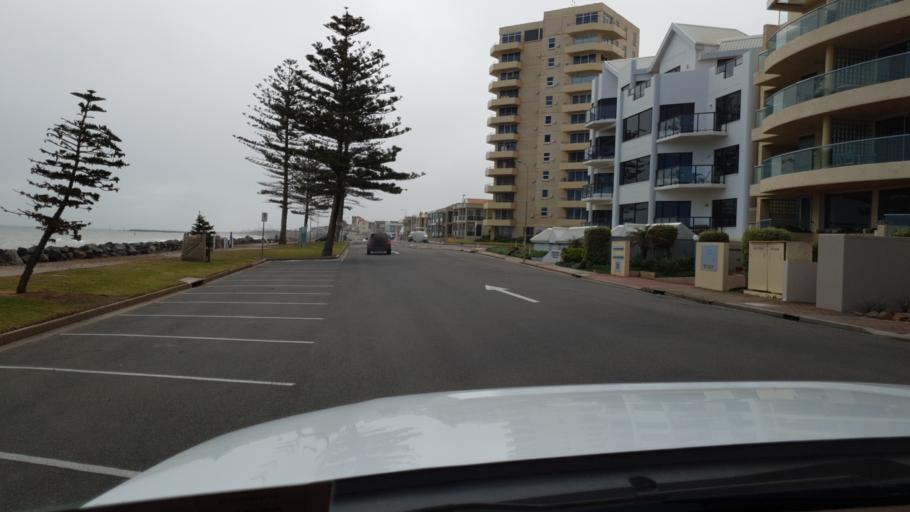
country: AU
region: South Australia
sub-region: Adelaide
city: Glenelg
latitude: -34.9727
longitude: 138.5111
